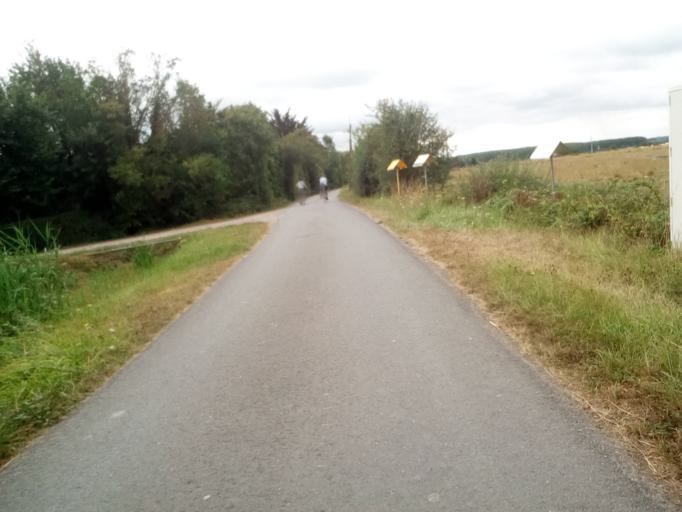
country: FR
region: Lower Normandy
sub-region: Departement du Calvados
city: Cabourg
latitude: 49.2587
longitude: -0.1327
